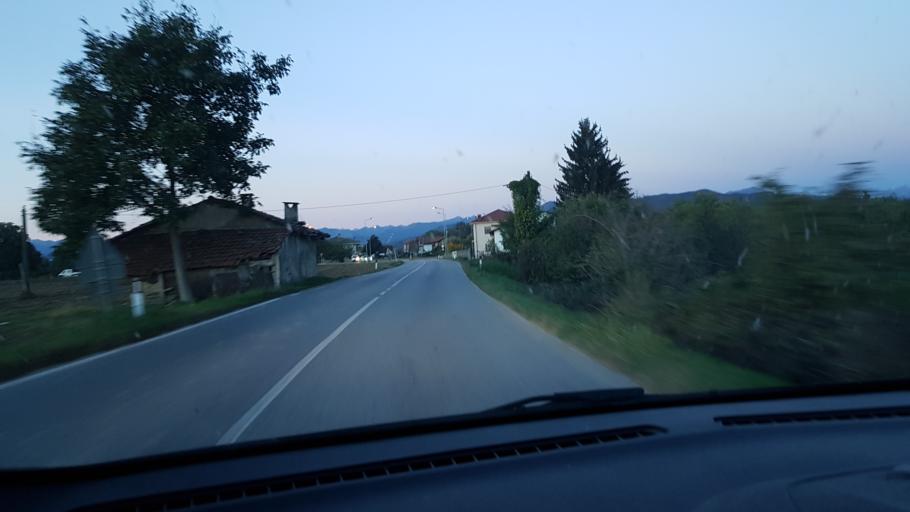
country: IT
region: Piedmont
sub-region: Provincia di Cuneo
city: Villafalletto
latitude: 44.5507
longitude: 7.5486
